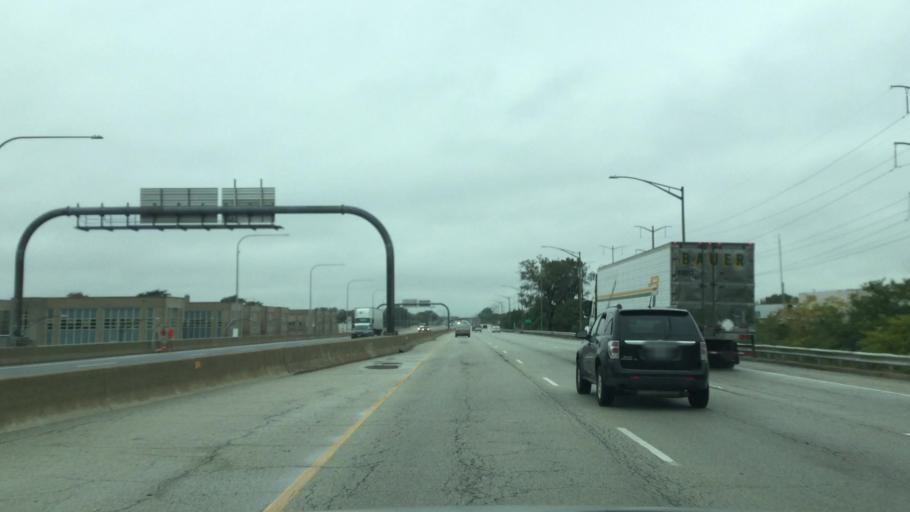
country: US
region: Indiana
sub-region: Lake County
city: Whiting
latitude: 41.7375
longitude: -87.5687
